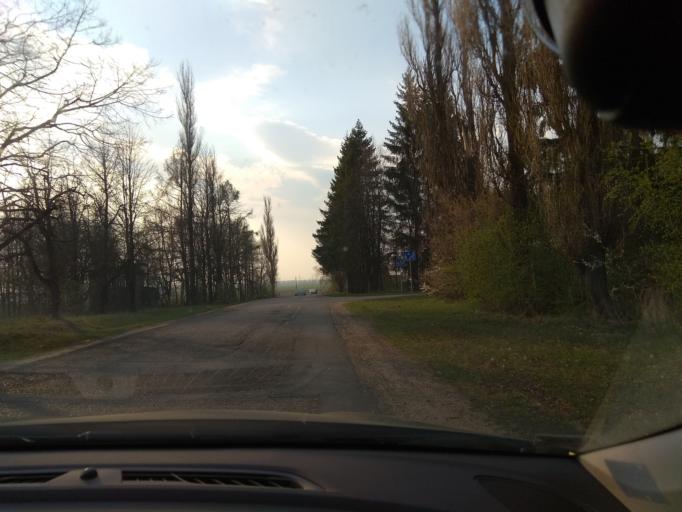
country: LT
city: Baltoji Voke
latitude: 54.5989
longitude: 25.1418
